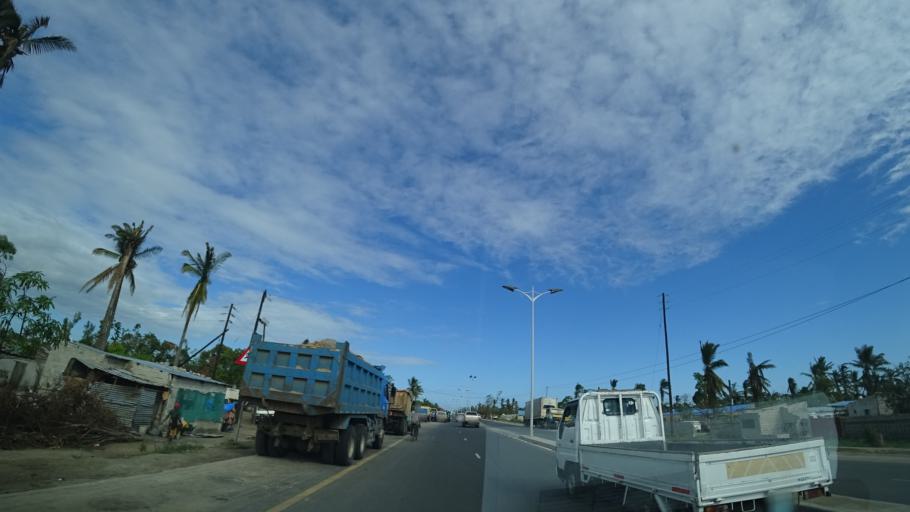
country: MZ
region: Sofala
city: Beira
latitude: -19.7577
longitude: 34.8782
